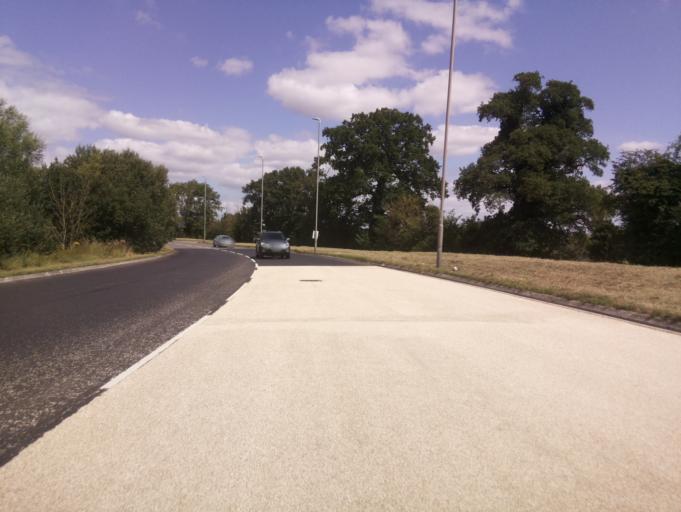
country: GB
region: England
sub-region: Buckinghamshire
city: Aylesbury
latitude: 51.8378
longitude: -0.8170
